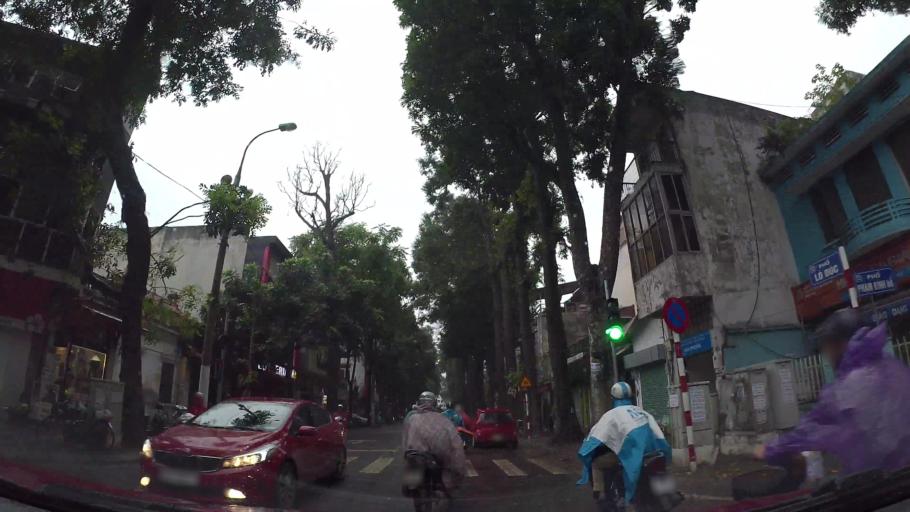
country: VN
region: Ha Noi
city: Hai BaTrung
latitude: 21.0160
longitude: 105.8564
